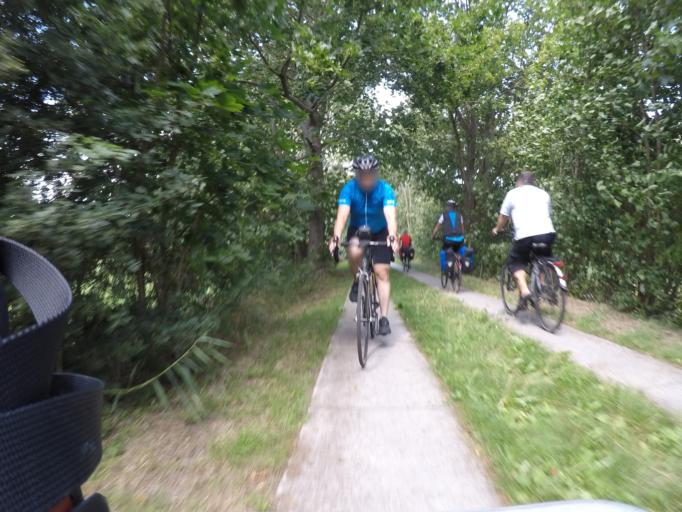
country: DE
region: Lower Saxony
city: Stelle
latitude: 53.4394
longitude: 10.1366
